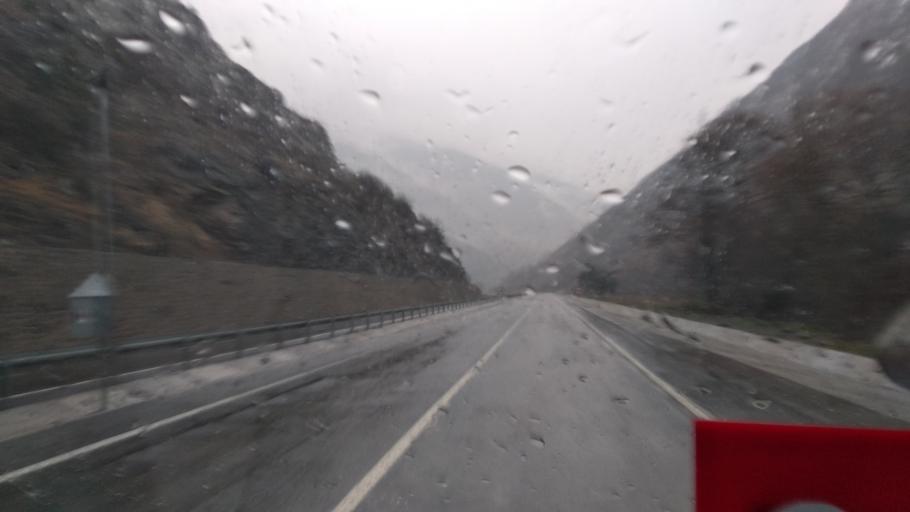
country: TR
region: Trabzon
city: Macka
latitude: 40.7931
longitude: 39.5821
